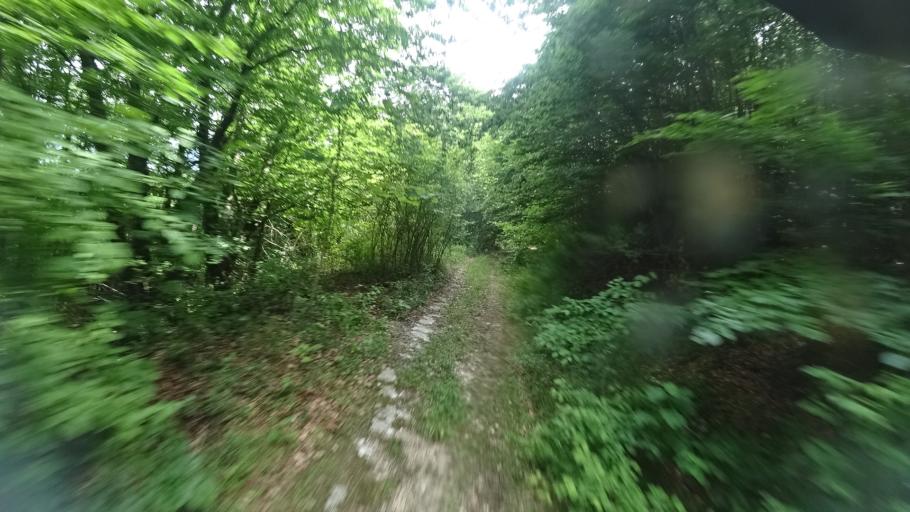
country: HR
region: Licko-Senjska
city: Jezerce
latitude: 44.8806
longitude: 15.7006
